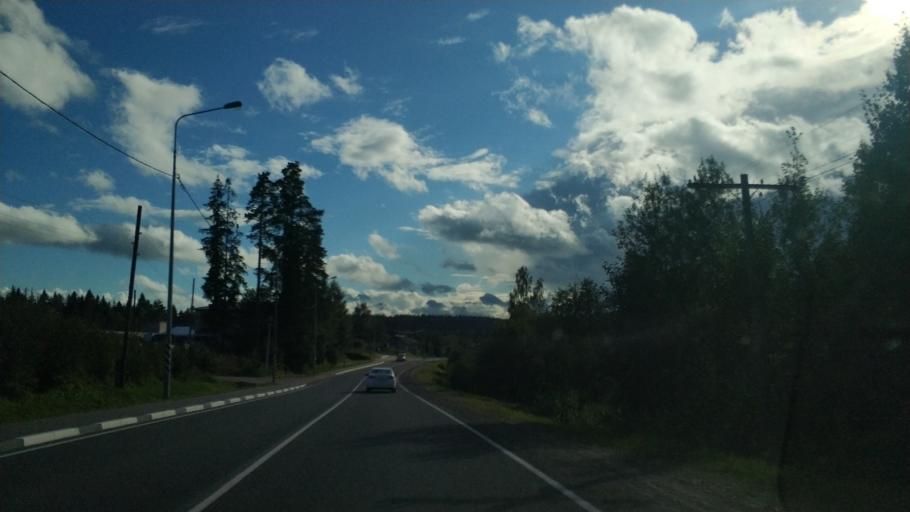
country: RU
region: Republic of Karelia
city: Lakhdenpokh'ya
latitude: 61.5209
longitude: 30.1579
